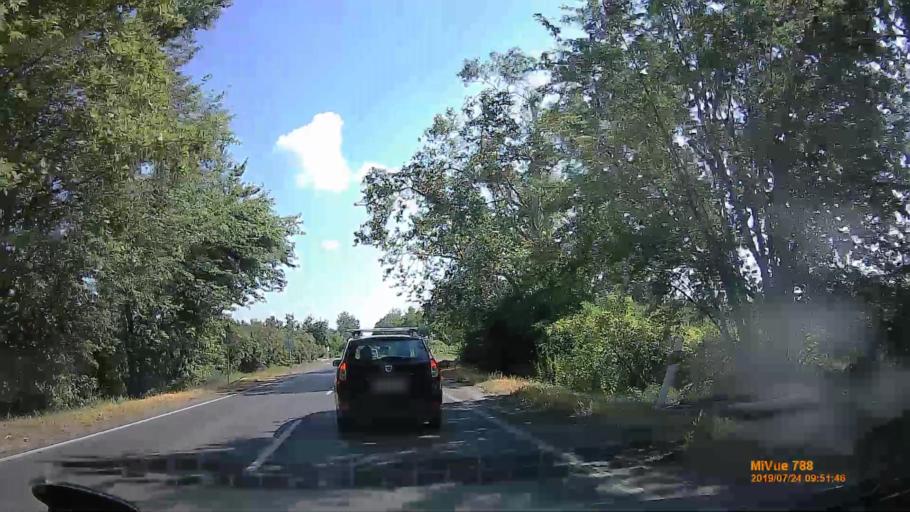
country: HU
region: Szabolcs-Szatmar-Bereg
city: Vaja
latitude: 48.0345
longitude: 22.1734
